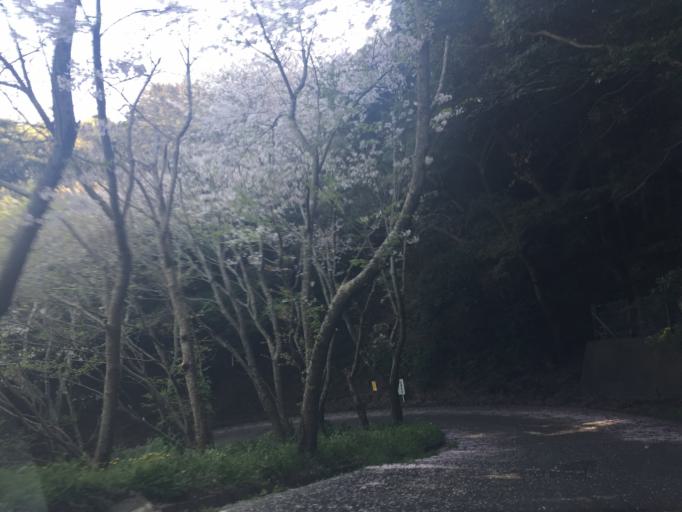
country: JP
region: Shizuoka
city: Kakegawa
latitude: 34.6784
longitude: 138.0330
